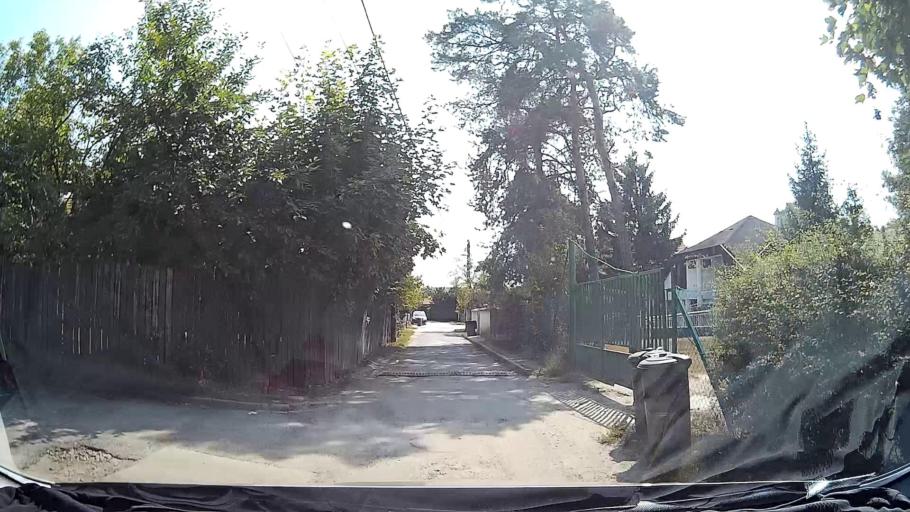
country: HU
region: Pest
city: Szentendre
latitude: 47.6799
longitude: 19.0525
